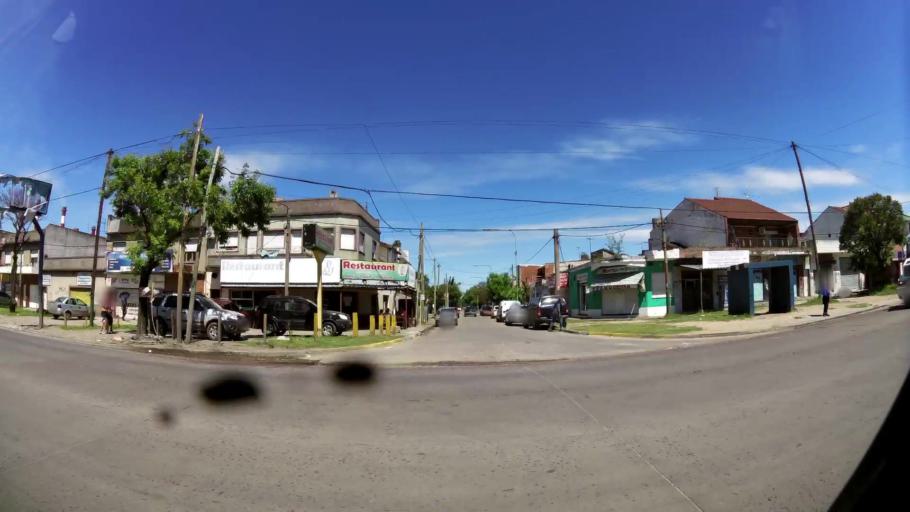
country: AR
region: Buenos Aires
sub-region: Partido de Almirante Brown
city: Adrogue
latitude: -34.7510
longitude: -58.3411
